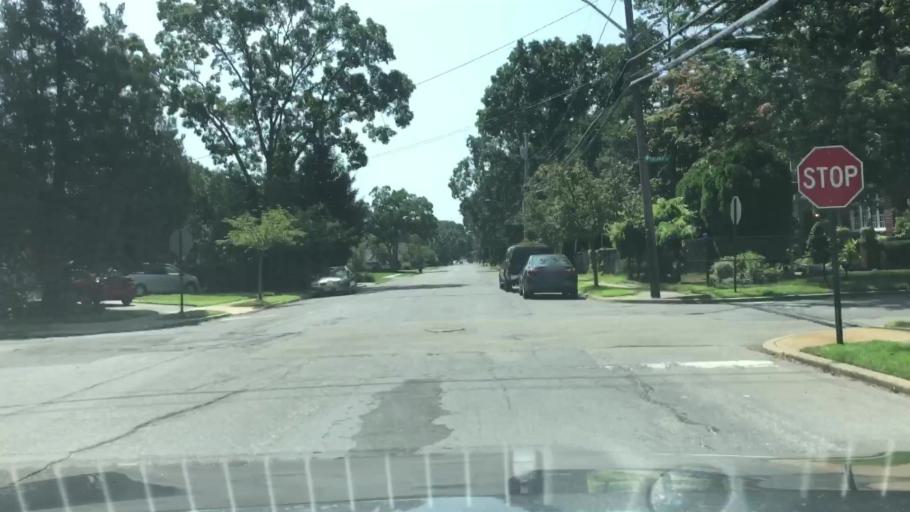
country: US
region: New York
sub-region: Nassau County
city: Massapequa
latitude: 40.6902
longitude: -73.4700
